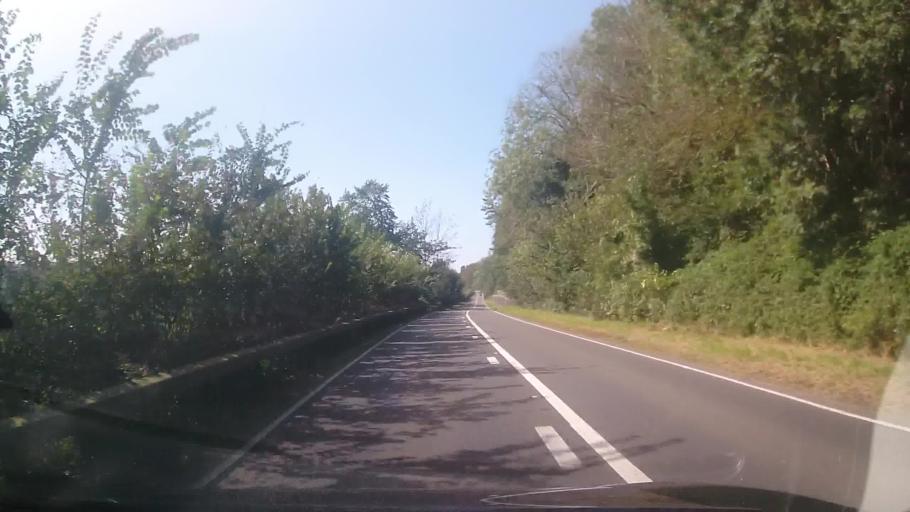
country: GB
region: Wales
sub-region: Carmarthenshire
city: Llanddarog
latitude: 51.8724
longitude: -4.2144
